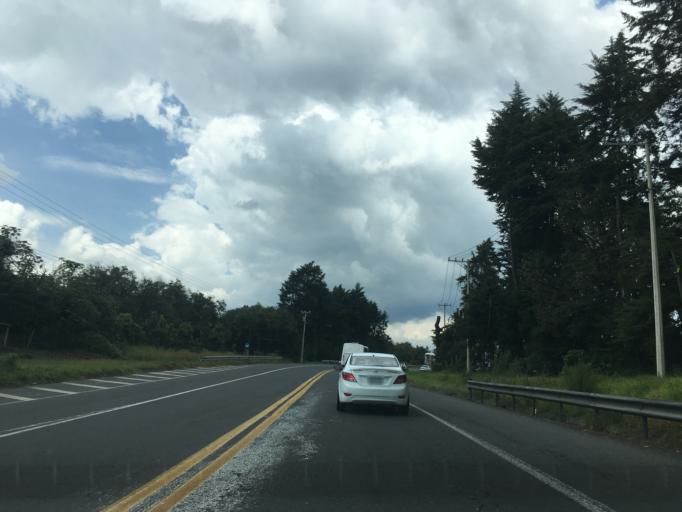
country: MX
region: Michoacan
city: Capacuaro
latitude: 19.4829
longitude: -102.0694
